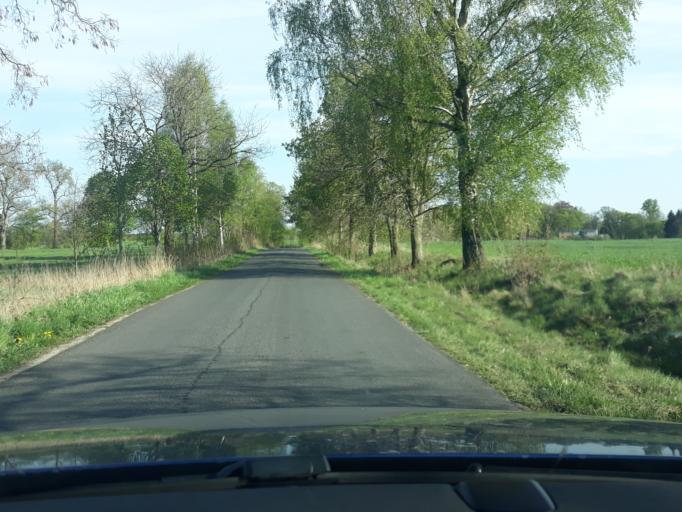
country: PL
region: Pomeranian Voivodeship
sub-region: Powiat czluchowski
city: Przechlewo
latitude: 53.8491
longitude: 17.3562
